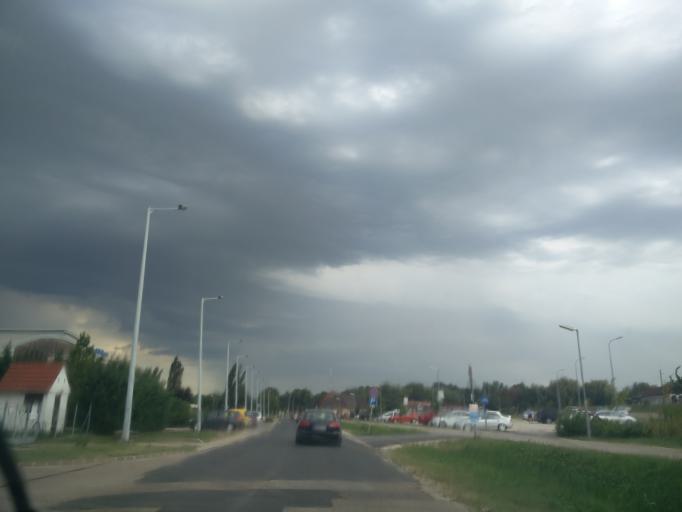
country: HU
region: Fejer
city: Velence
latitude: 47.2260
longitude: 18.6611
